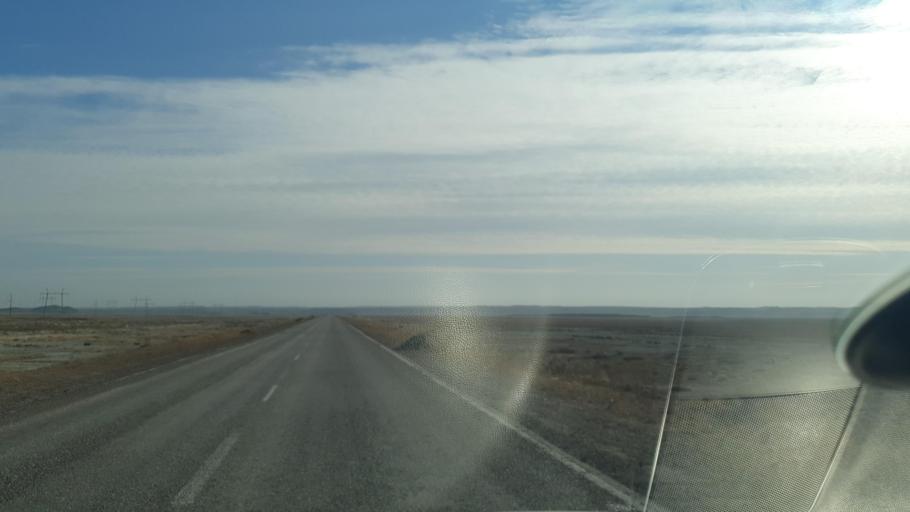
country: KZ
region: Zhambyl
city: Mynaral
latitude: 45.5867
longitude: 73.4047
